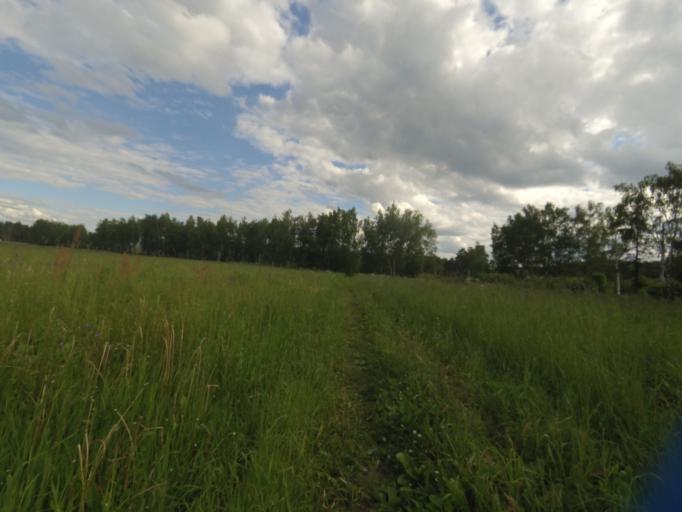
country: RU
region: Moskovskaya
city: Nekrasovskiy
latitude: 56.1066
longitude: 37.5150
